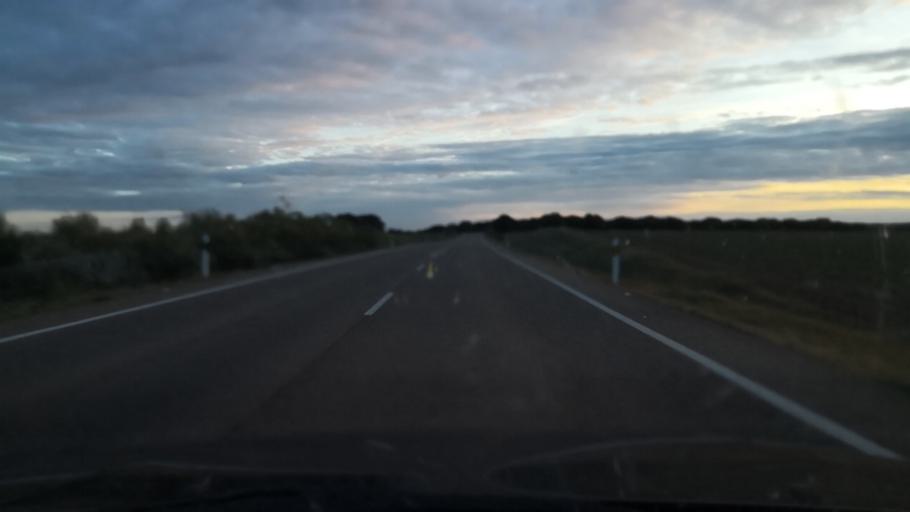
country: ES
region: Extremadura
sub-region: Provincia de Badajoz
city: Villar del Rey
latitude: 39.0492
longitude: -6.8018
